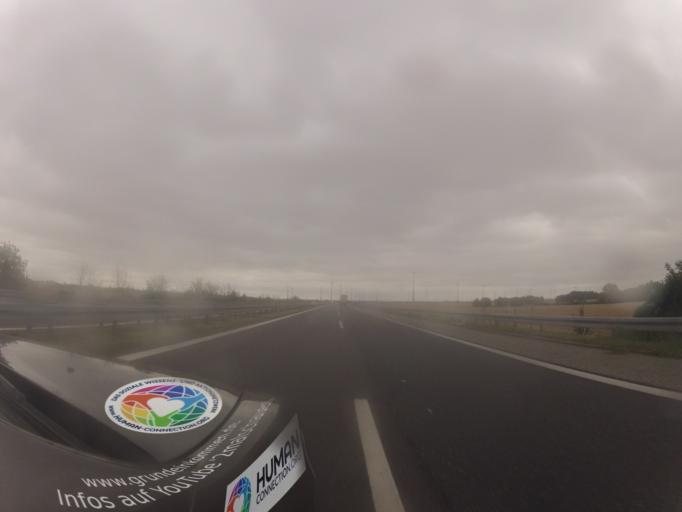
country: DE
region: Brandenburg
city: Schonfeld
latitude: 53.4095
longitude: 13.9959
